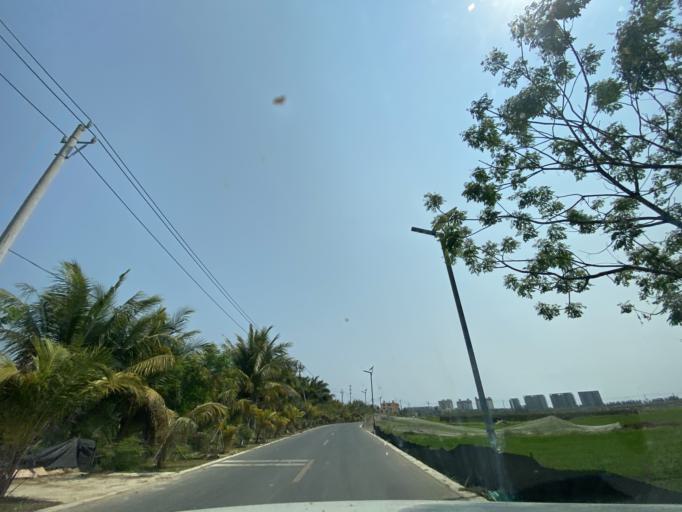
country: CN
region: Hainan
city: Yingzhou
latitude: 18.4135
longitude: 109.8150
